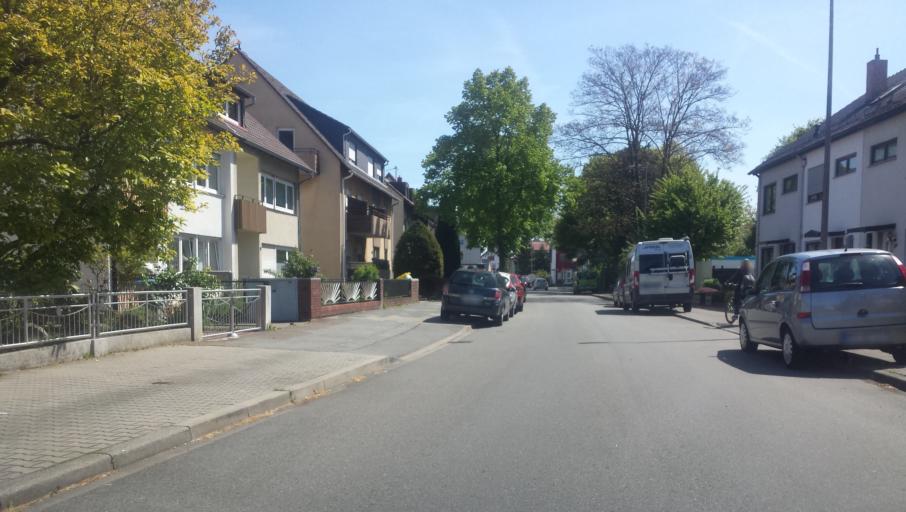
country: DE
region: Baden-Wuerttemberg
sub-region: Karlsruhe Region
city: Ilvesheim
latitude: 49.4986
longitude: 8.5416
